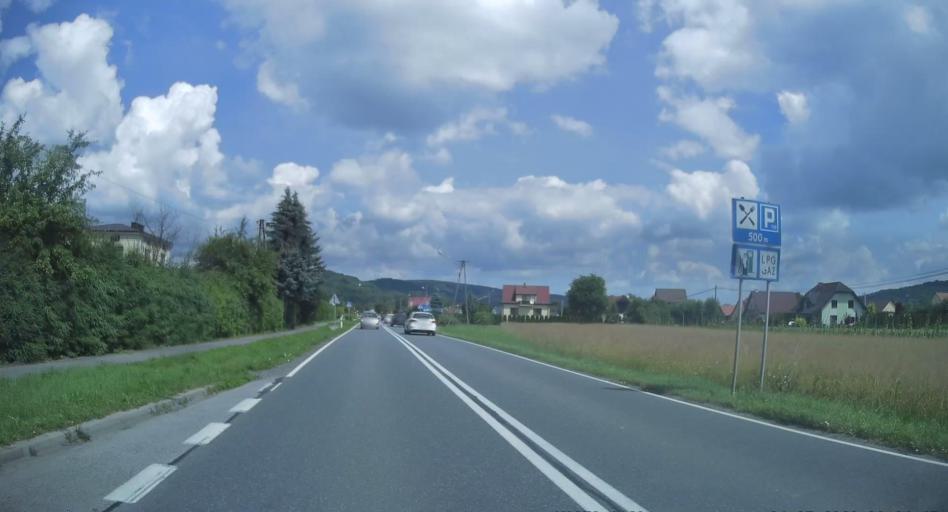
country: PL
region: Lesser Poland Voivodeship
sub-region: Powiat tarnowski
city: Zakliczyn
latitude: 49.8930
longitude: 20.8170
